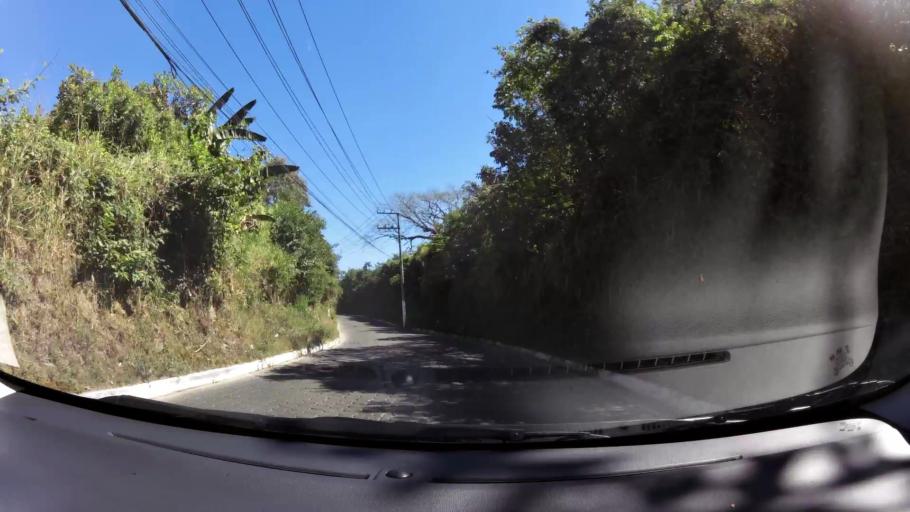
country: SV
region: San Salvador
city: Apopa
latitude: 13.8051
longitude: -89.1869
